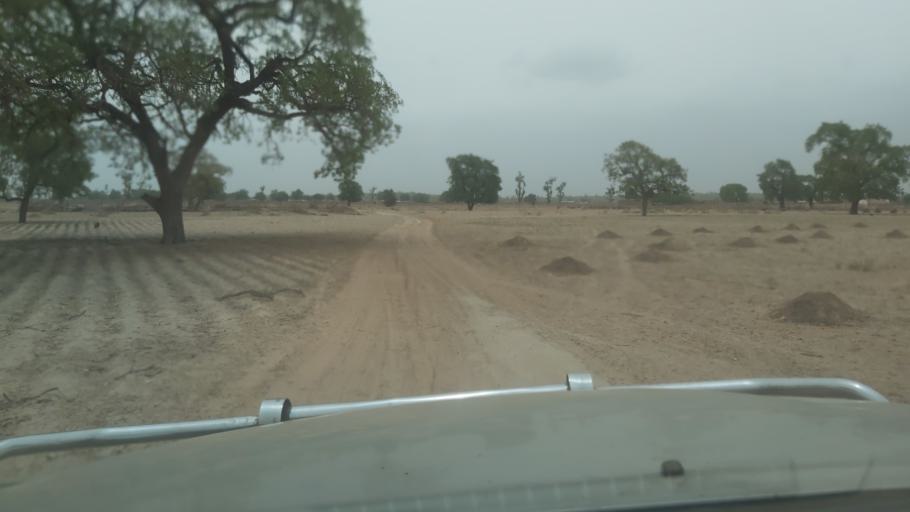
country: ML
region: Koulikoro
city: Banamba
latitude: 13.3769
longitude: -7.2286
